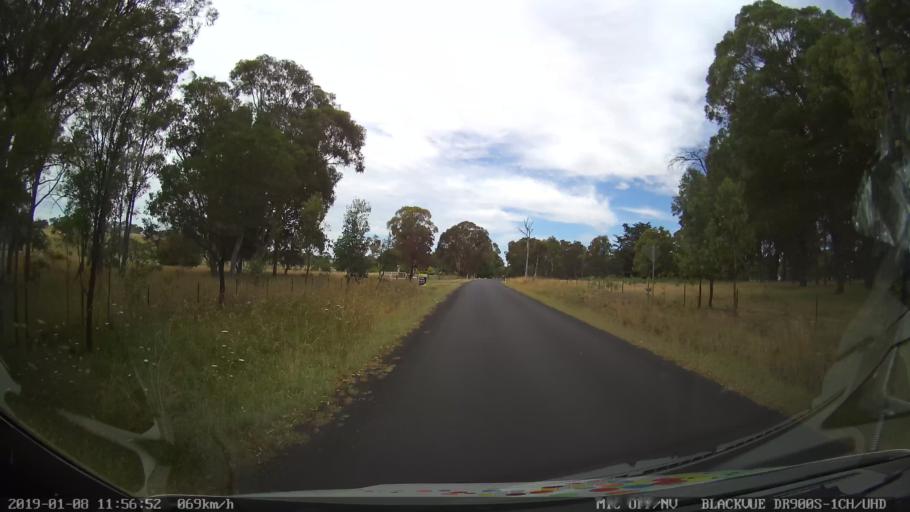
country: AU
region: New South Wales
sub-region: Armidale Dumaresq
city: Armidale
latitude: -30.4446
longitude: 151.5650
